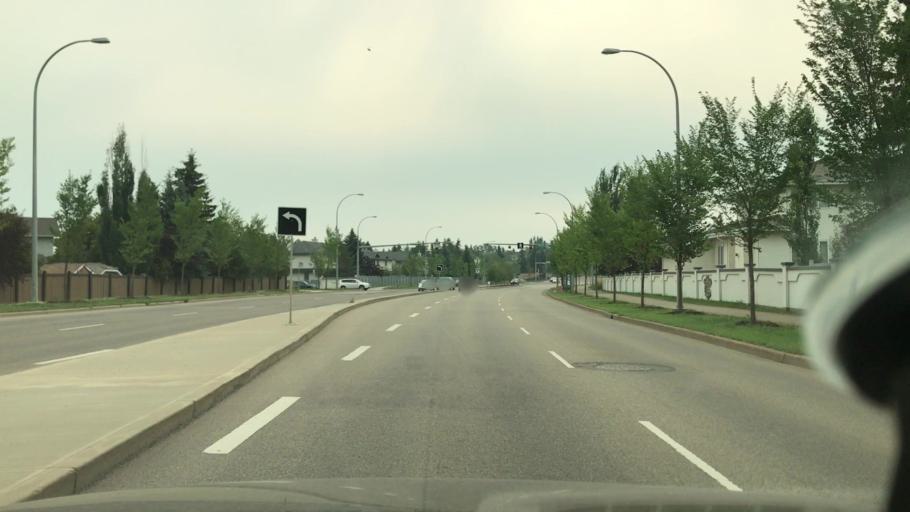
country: CA
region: Alberta
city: Edmonton
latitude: 53.4673
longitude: -113.5766
